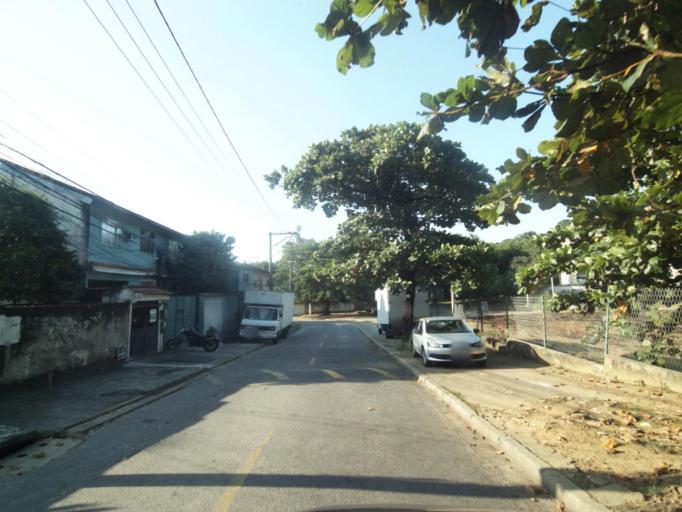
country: BR
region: Rio de Janeiro
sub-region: Niteroi
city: Niteroi
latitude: -22.8861
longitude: -43.0933
